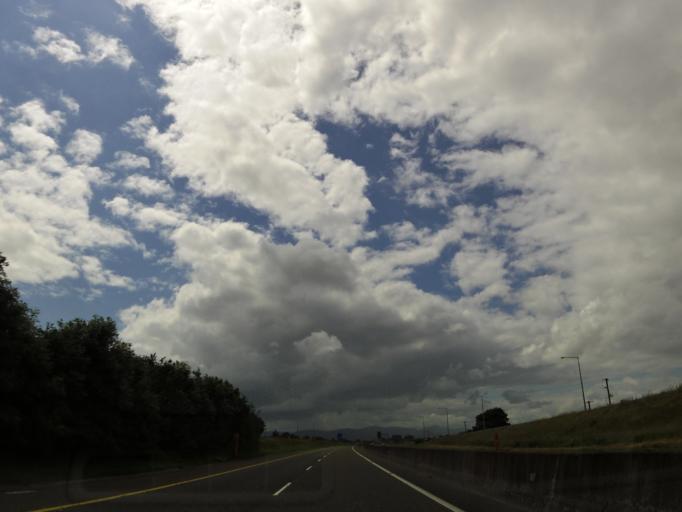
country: IE
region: Munster
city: Cashel
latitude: 52.5080
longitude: -7.8721
